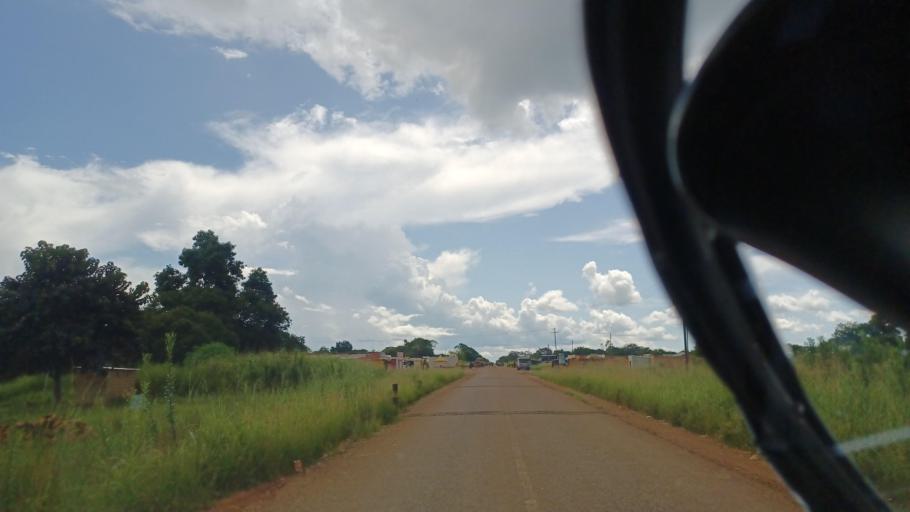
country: ZM
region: North-Western
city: Kasempa
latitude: -13.1037
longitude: 25.8725
